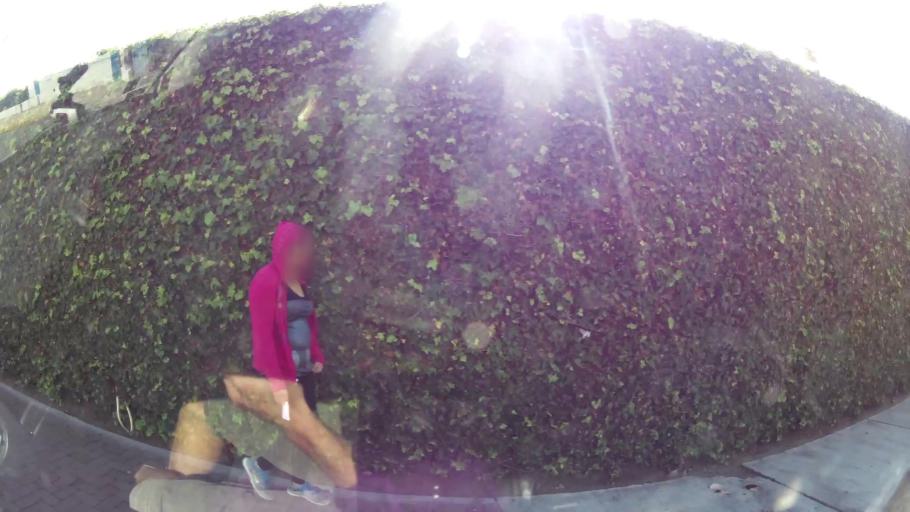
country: EC
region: Pichincha
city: Quito
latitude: -0.1996
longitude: -78.4330
